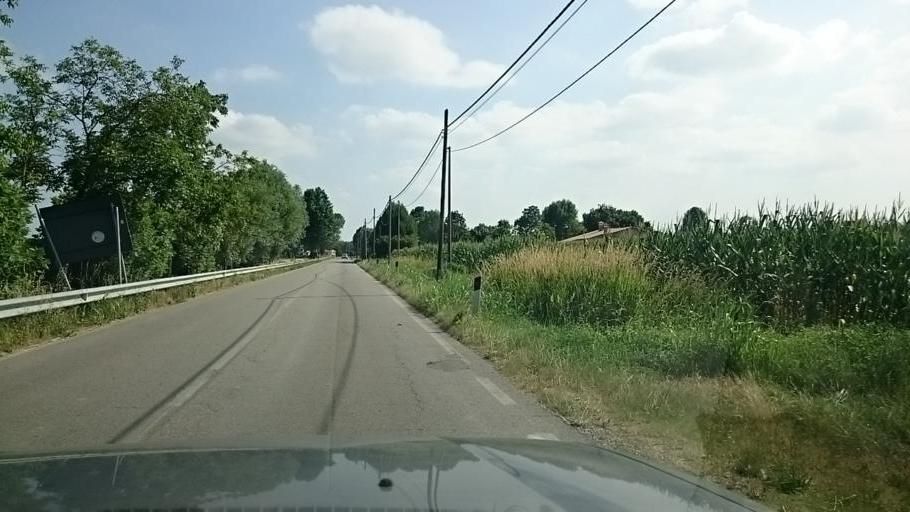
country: IT
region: Veneto
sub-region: Provincia di Padova
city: Villa del Conte
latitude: 45.5808
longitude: 11.8661
